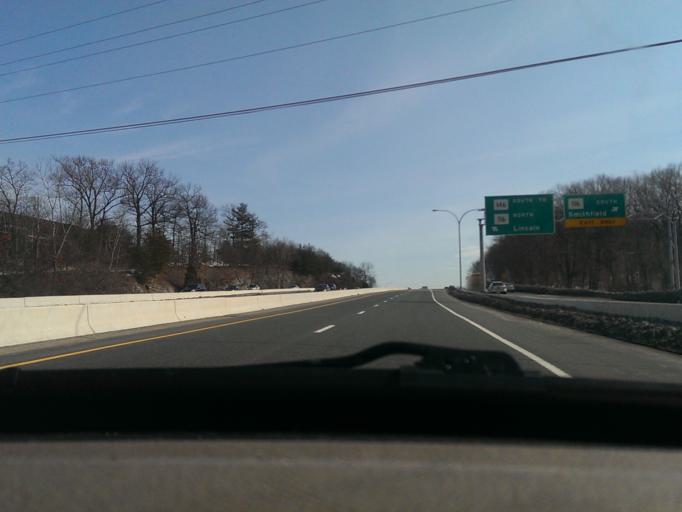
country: US
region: Rhode Island
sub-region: Providence County
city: Cumberland Hill
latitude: 41.9392
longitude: -71.4714
